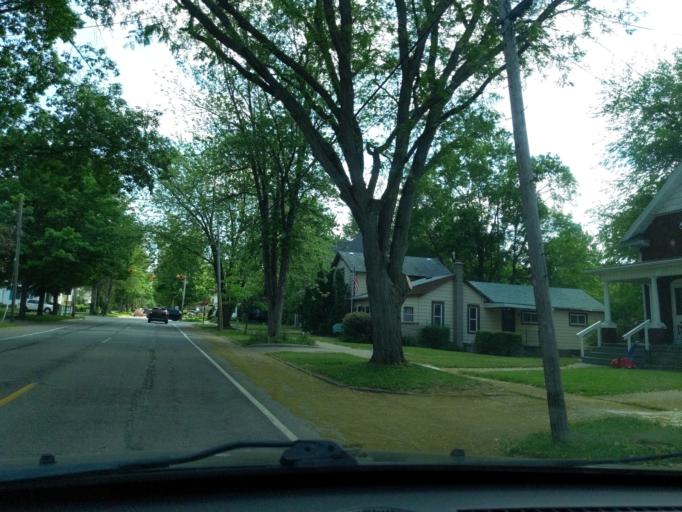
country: US
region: Michigan
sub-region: Clinton County
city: Saint Johns
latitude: 43.0022
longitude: -84.5626
